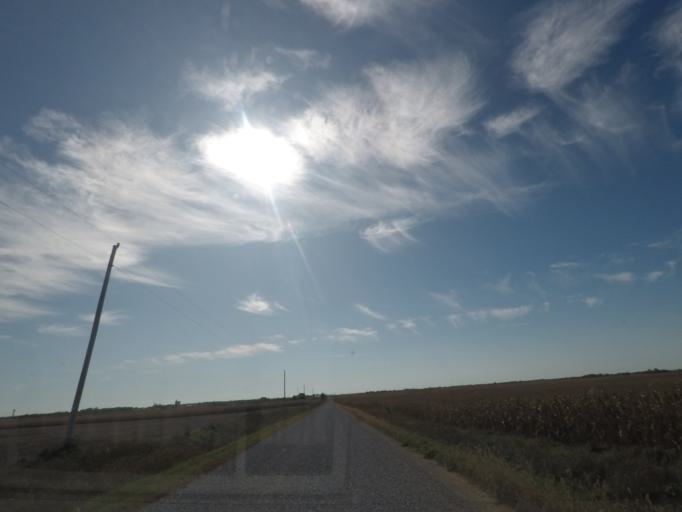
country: US
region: Iowa
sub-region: Story County
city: Nevada
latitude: 42.0470
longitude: -93.3289
